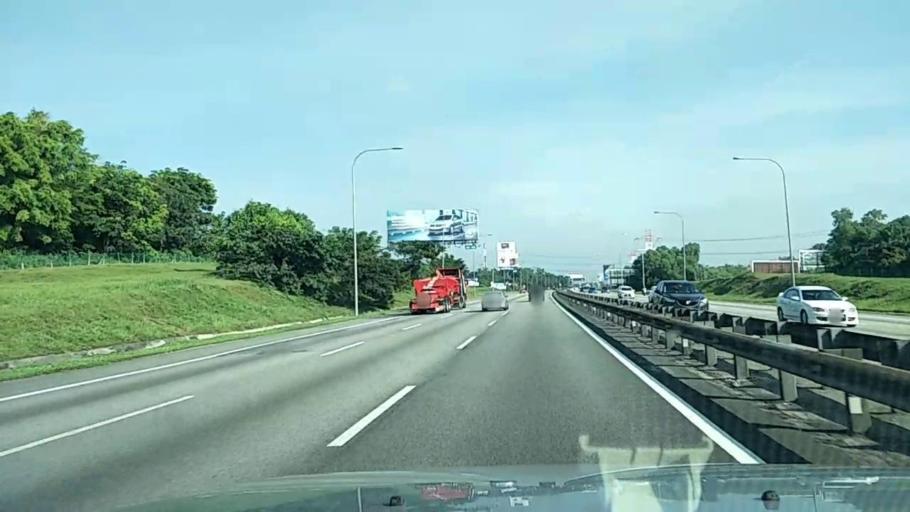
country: MY
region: Putrajaya
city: Putrajaya
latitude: 2.8575
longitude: 101.6468
